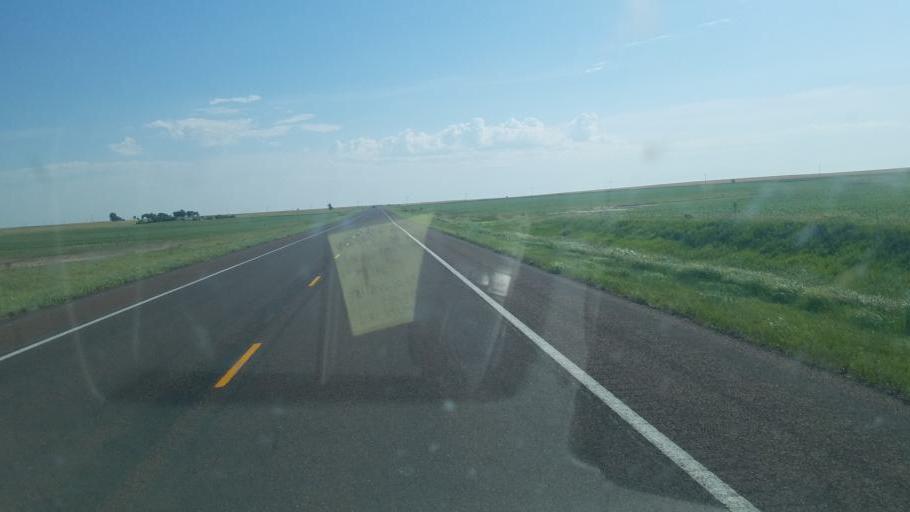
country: US
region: Kansas
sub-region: Barton County
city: Ellinwood
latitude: 38.5664
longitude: -98.4496
